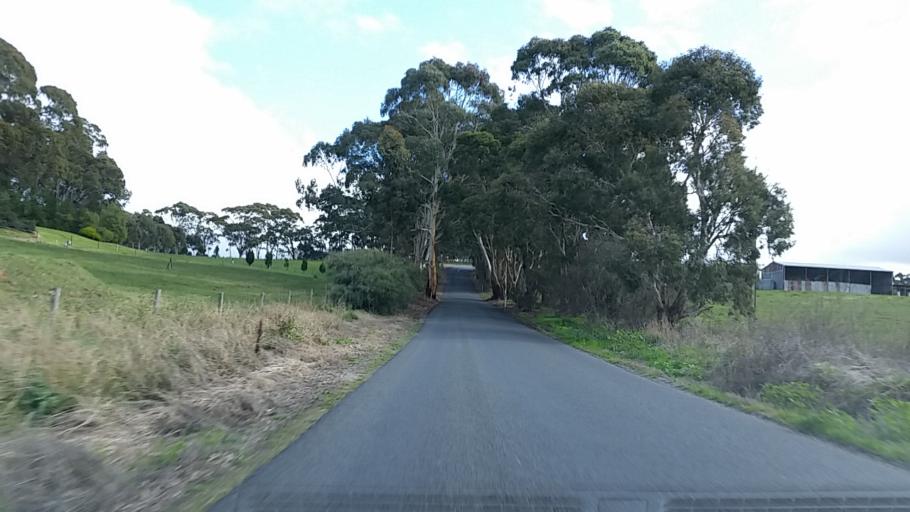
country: AU
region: South Australia
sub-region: Mount Barker
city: Little Hampton
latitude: -35.0797
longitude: 138.8228
